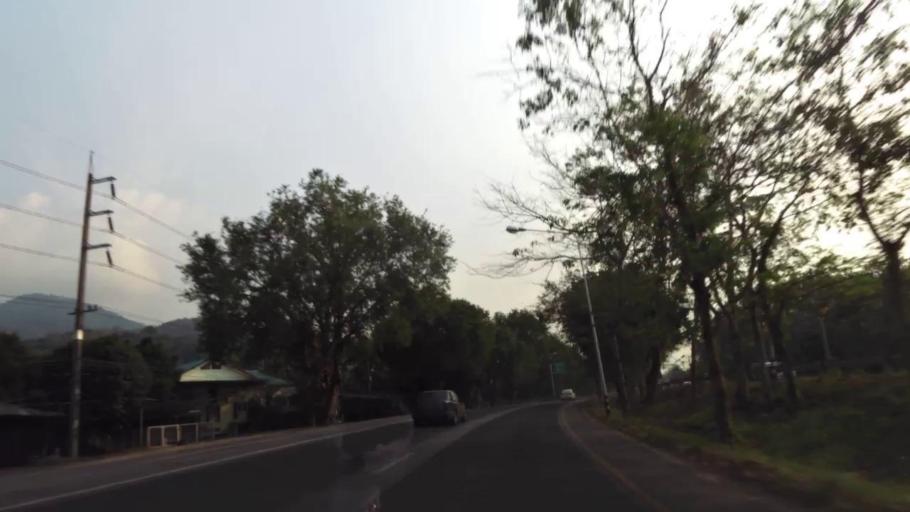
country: TH
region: Chanthaburi
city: Chanthaburi
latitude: 12.5706
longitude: 102.1626
